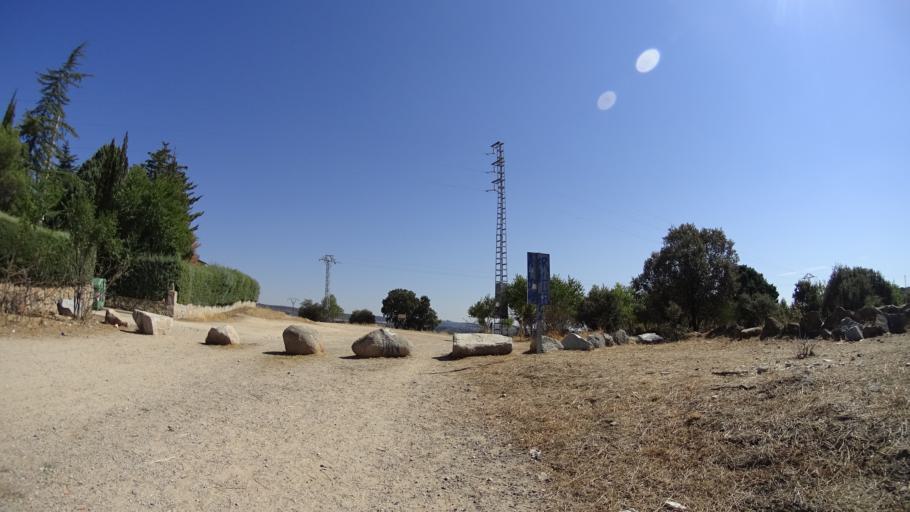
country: ES
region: Madrid
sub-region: Provincia de Madrid
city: Collado-Villalba
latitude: 40.6128
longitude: -4.0113
